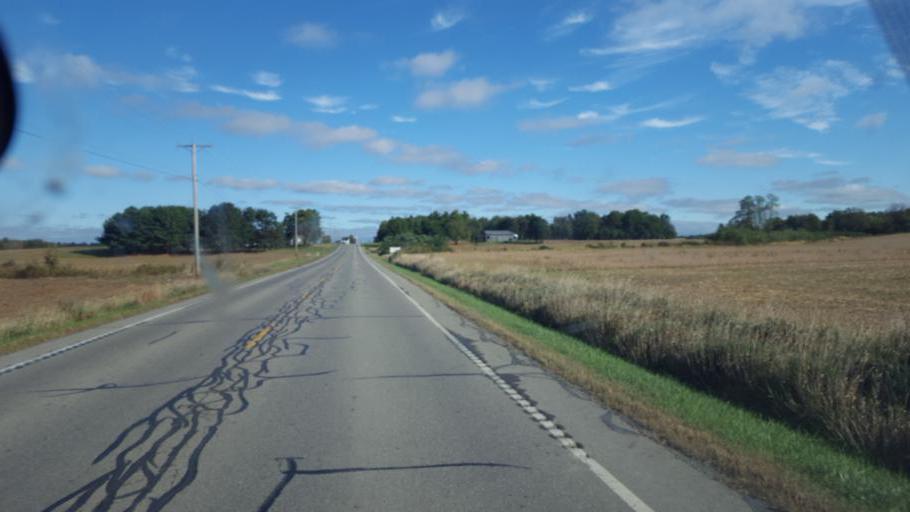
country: US
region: Ohio
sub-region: Huron County
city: Greenwich
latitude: 40.9873
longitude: -82.4885
